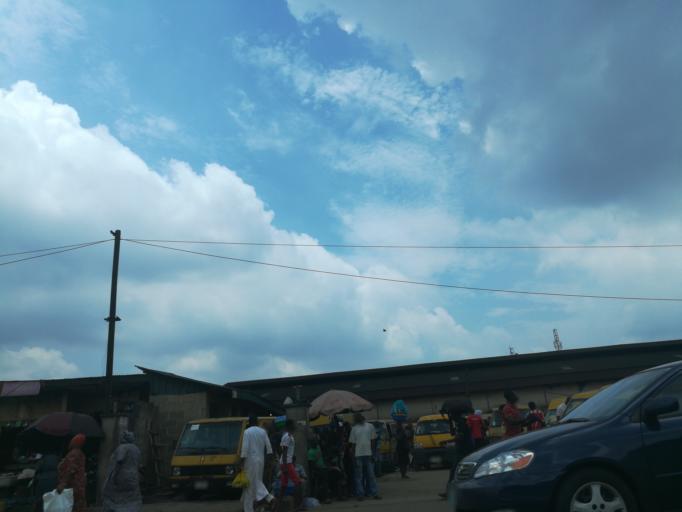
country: NG
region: Lagos
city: Ojota
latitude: 6.5888
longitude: 3.3781
